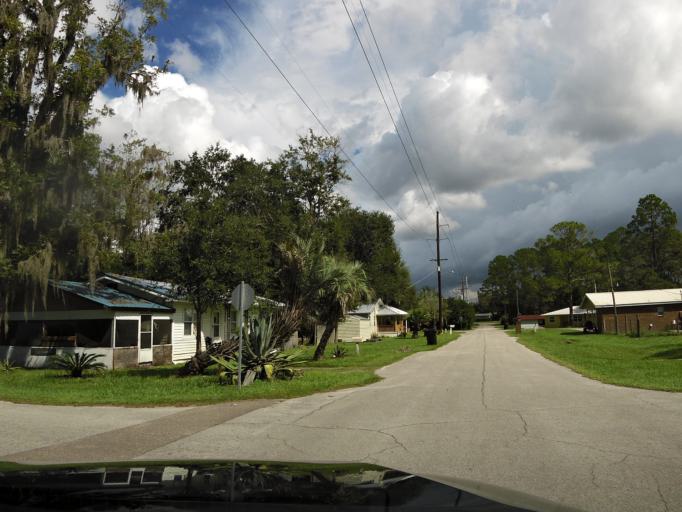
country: US
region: Florida
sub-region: Union County
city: Lake Butler
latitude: 30.0195
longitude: -82.3406
